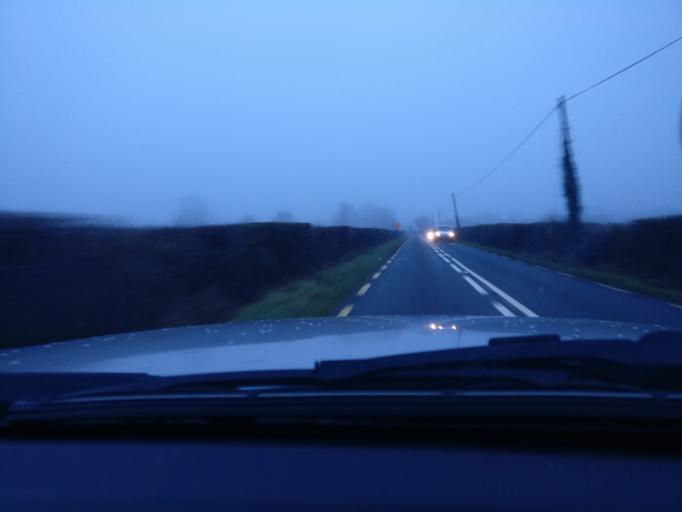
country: IE
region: Leinster
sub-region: An Mhi
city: Ballivor
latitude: 53.6047
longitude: -6.9917
